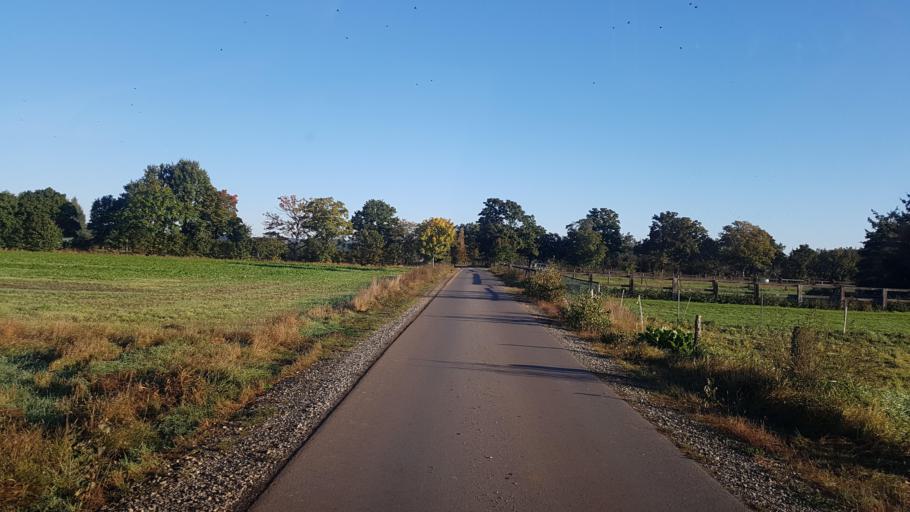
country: DE
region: Brandenburg
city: Hohenleipisch
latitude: 51.4680
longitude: 13.5632
